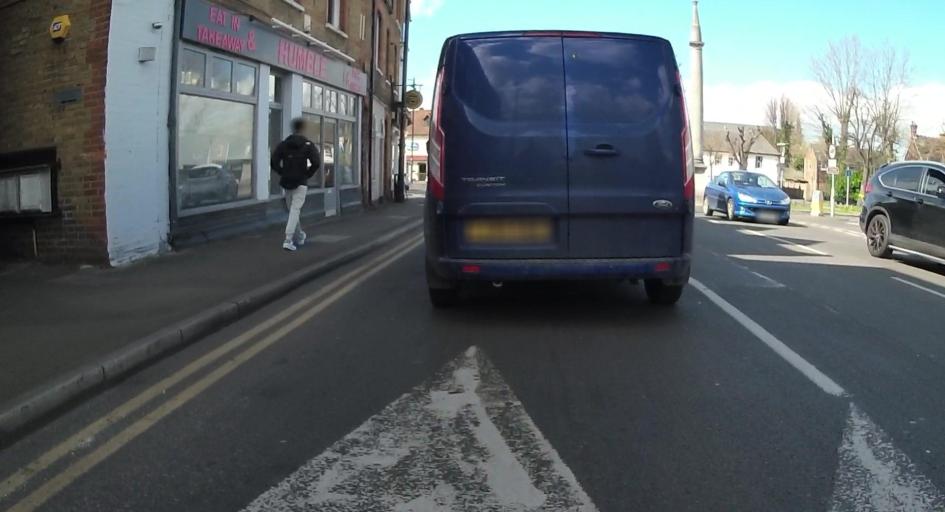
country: GB
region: England
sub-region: Surrey
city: Weybridge
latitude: 51.3734
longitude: -0.4551
